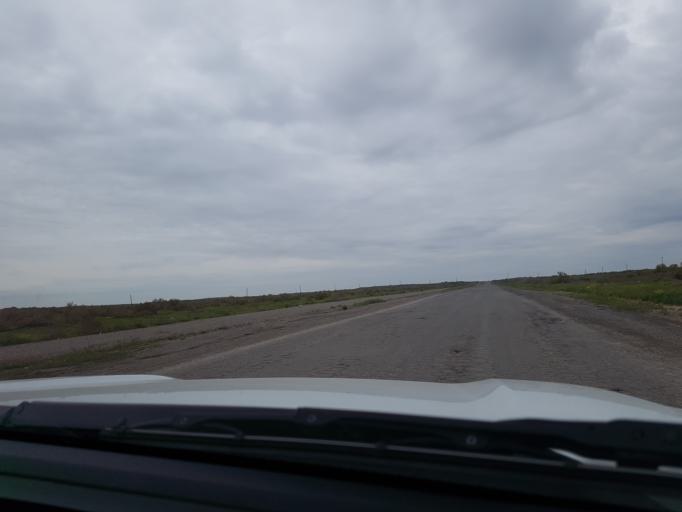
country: TM
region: Mary
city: Bayramaly
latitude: 37.9231
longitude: 62.6243
